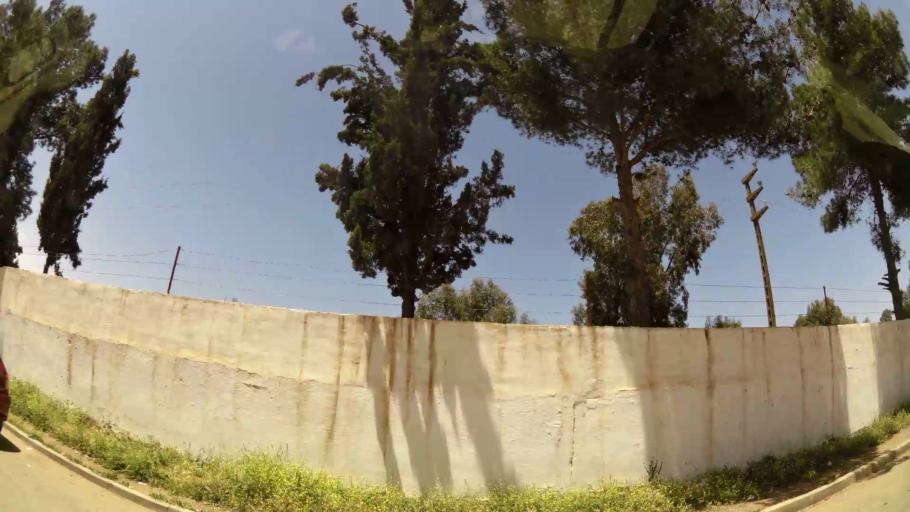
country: MA
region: Rabat-Sale-Zemmour-Zaer
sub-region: Khemisset
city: Khemisset
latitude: 33.8292
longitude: -6.0916
